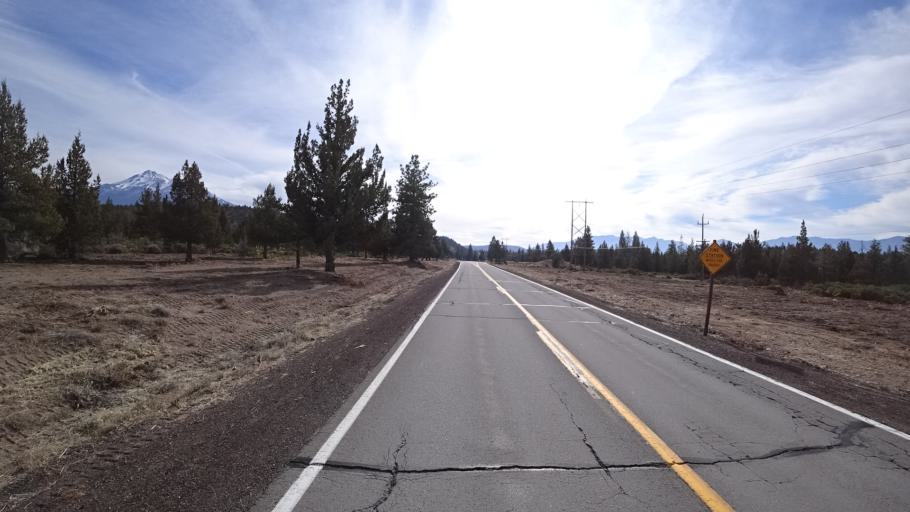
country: US
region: California
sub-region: Siskiyou County
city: Weed
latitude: 41.5306
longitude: -122.3647
